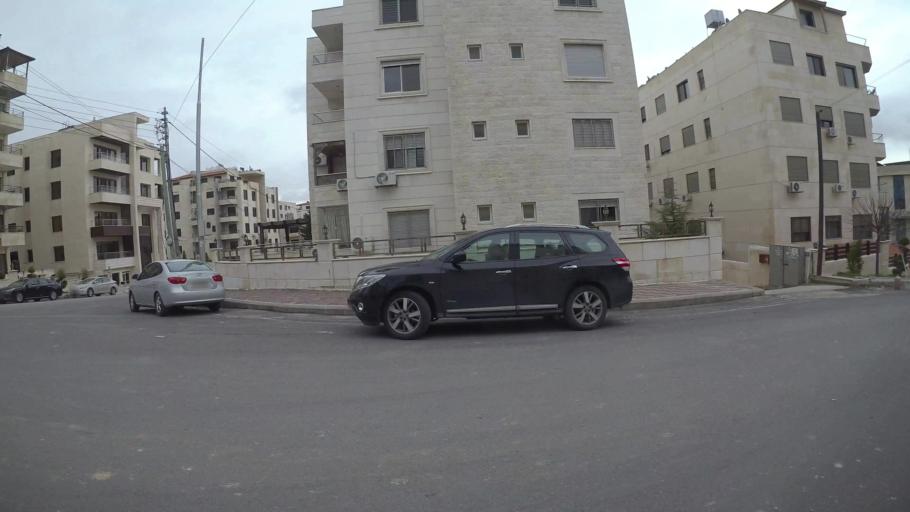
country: JO
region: Amman
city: Al Jubayhah
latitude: 31.9935
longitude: 35.8378
